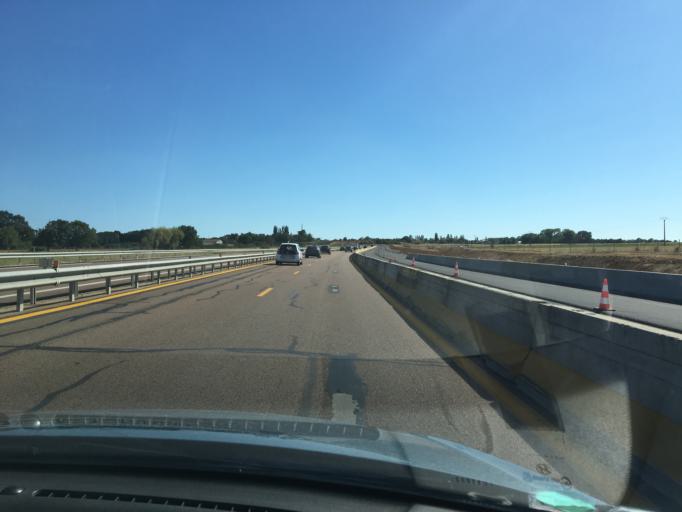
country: FR
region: Bourgogne
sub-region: Departement de l'Yonne
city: Venoy
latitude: 47.8258
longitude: 3.6239
